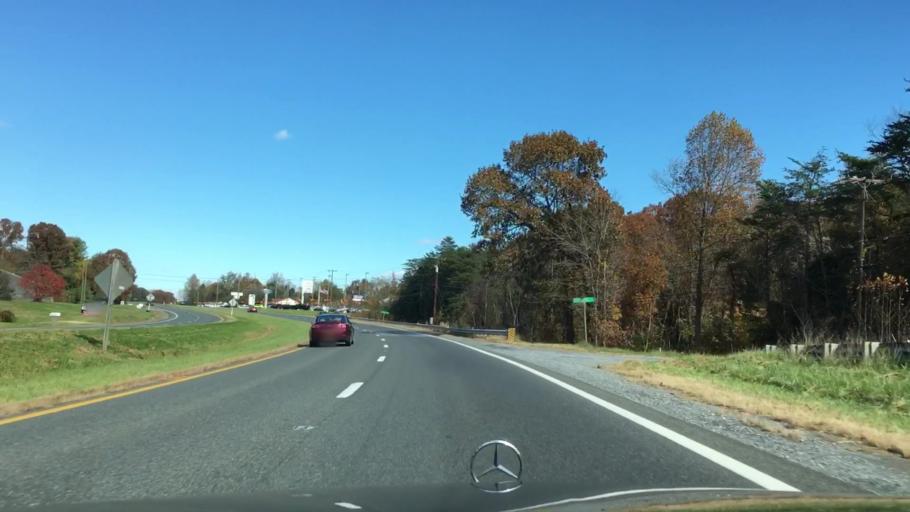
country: US
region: Virginia
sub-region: Campbell County
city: Altavista
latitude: 37.1491
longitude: -79.2288
